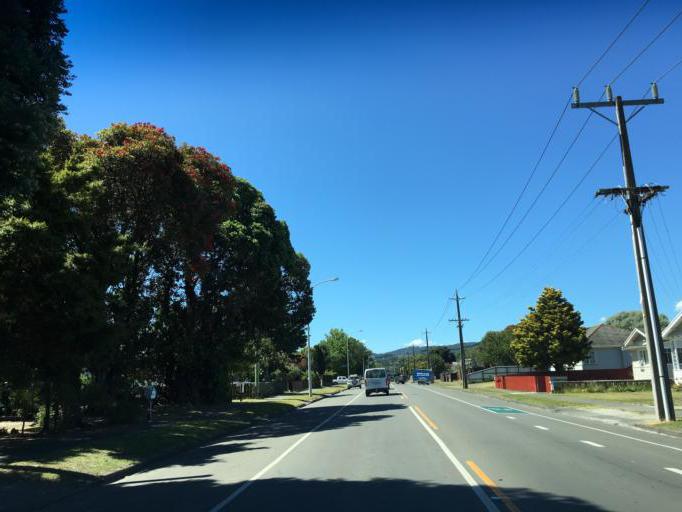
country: NZ
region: Gisborne
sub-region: Gisborne District
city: Gisborne
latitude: -38.6635
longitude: 178.0064
